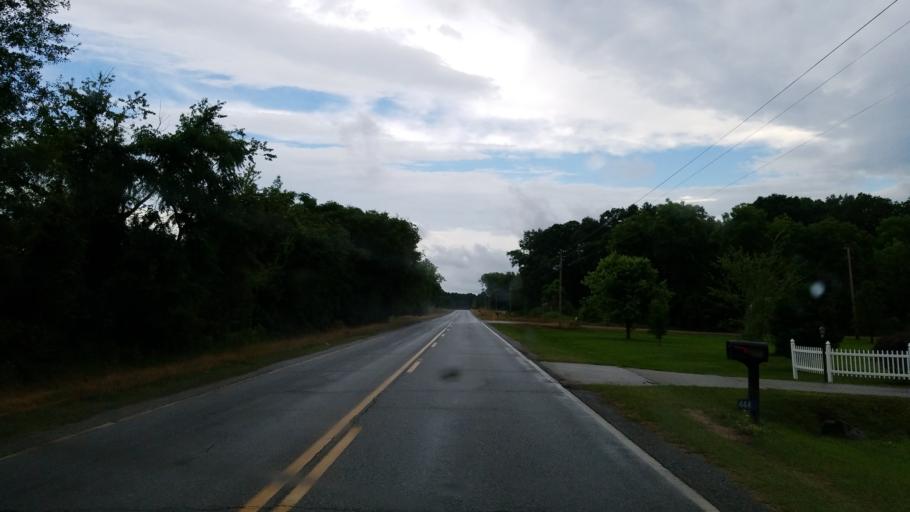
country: US
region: Georgia
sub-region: Crisp County
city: Cordele
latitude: 31.8865
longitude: -83.7674
